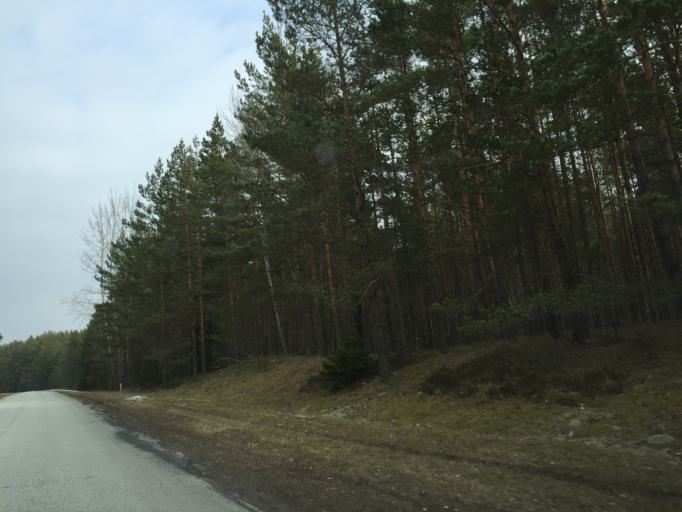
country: LV
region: Salacgrivas
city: Ainazi
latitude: 57.9589
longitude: 24.4020
